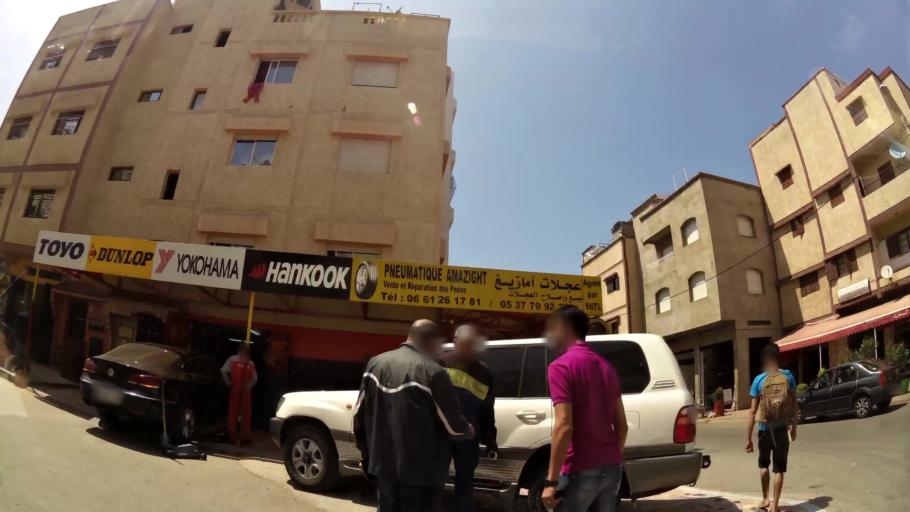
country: MA
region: Rabat-Sale-Zemmour-Zaer
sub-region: Skhirate-Temara
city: Temara
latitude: 33.9706
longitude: -6.8869
